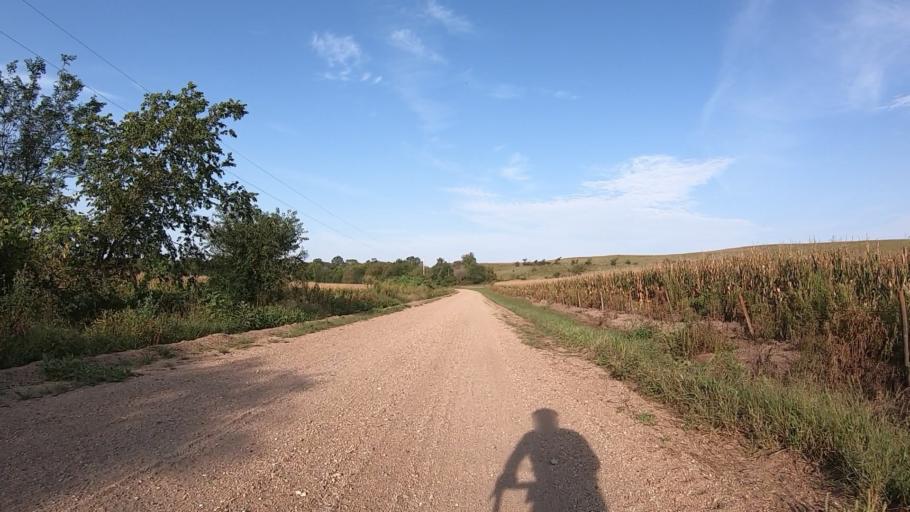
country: US
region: Kansas
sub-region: Marshall County
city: Blue Rapids
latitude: 39.6679
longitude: -96.8102
